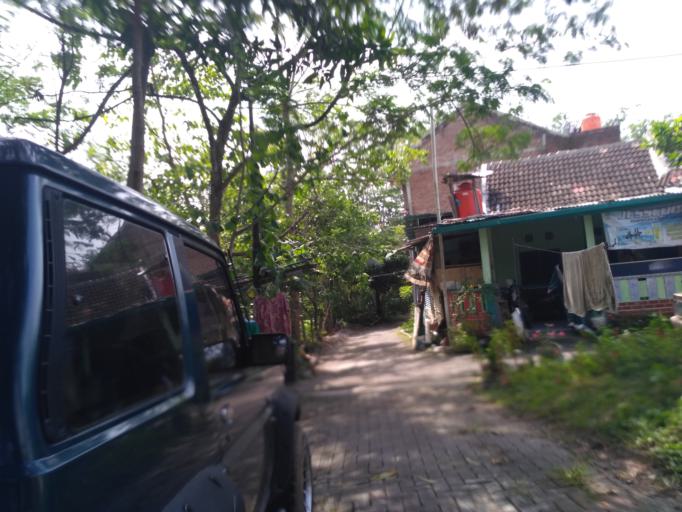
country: ID
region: Central Java
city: Semarang
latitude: -7.0391
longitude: 110.4365
